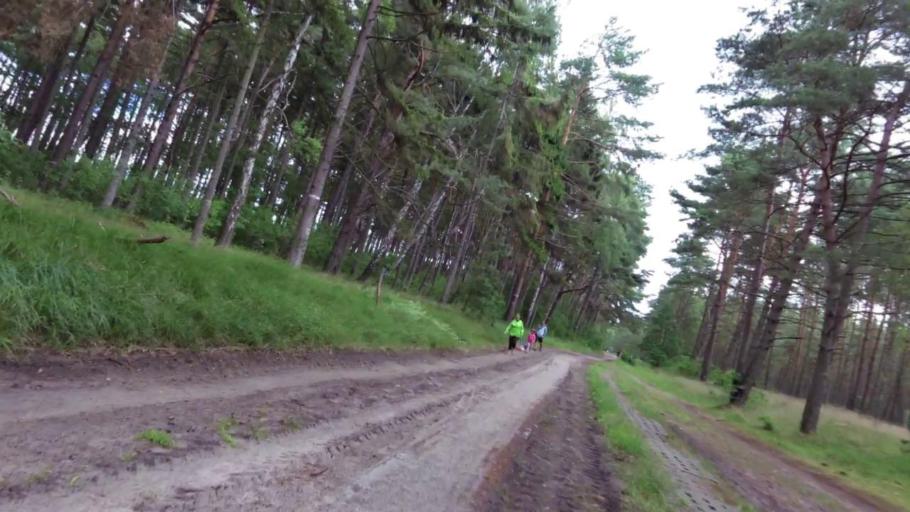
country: PL
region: West Pomeranian Voivodeship
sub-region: Powiat slawienski
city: Darlowo
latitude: 54.5025
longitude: 16.4587
